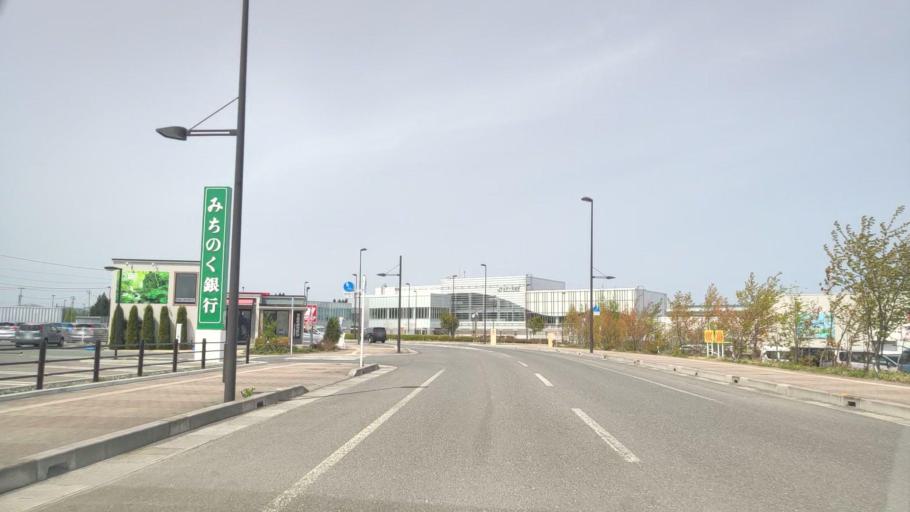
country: JP
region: Aomori
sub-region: Misawa Shi
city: Inuotose
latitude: 40.7182
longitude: 141.1540
